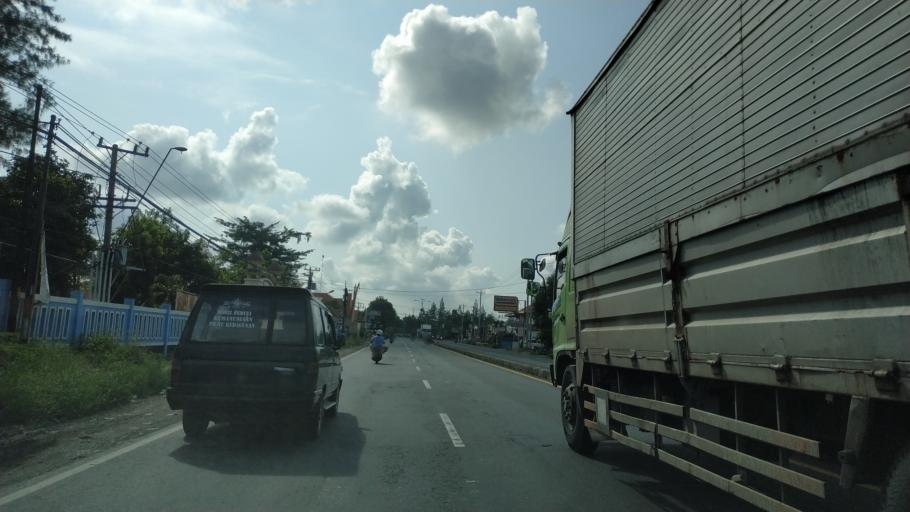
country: ID
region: Central Java
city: Comal
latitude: -6.8982
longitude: 109.5361
